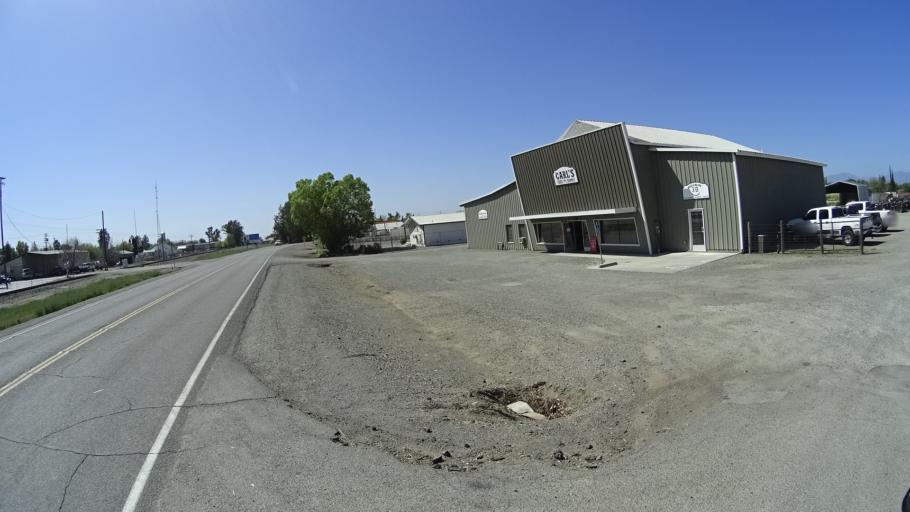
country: US
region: California
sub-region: Glenn County
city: Willows
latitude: 39.5297
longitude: -122.1935
